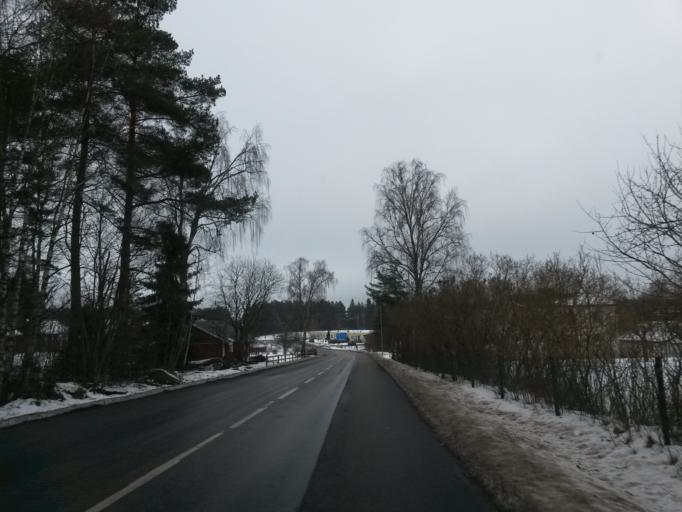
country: SE
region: Vaestra Goetaland
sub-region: Herrljunga Kommun
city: Herrljunga
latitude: 57.9886
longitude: 13.0853
